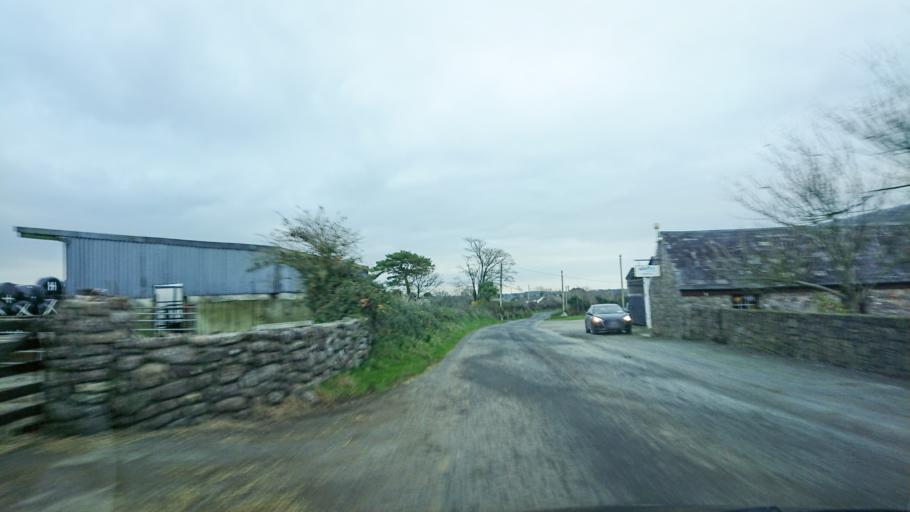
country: IE
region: Munster
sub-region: Waterford
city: Dunmore East
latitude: 52.2387
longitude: -6.9818
